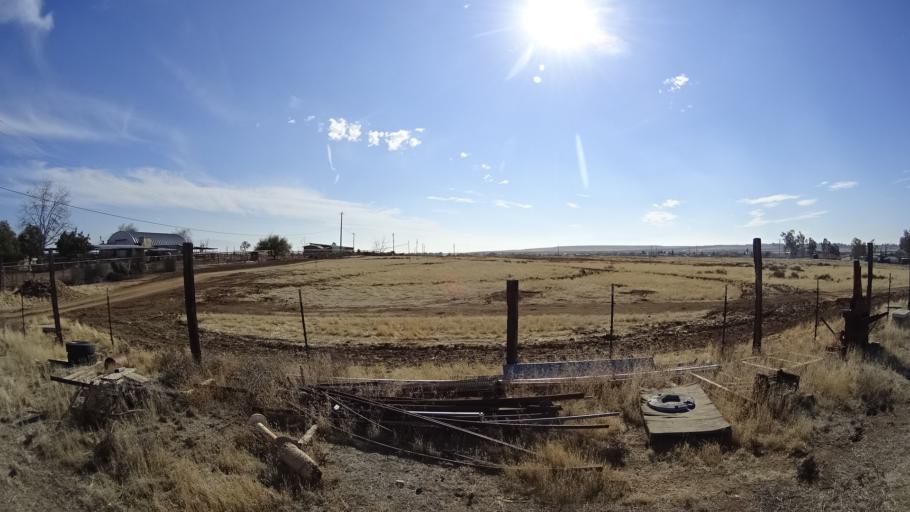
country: US
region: California
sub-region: Kern County
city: Oildale
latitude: 35.4163
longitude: -118.8964
